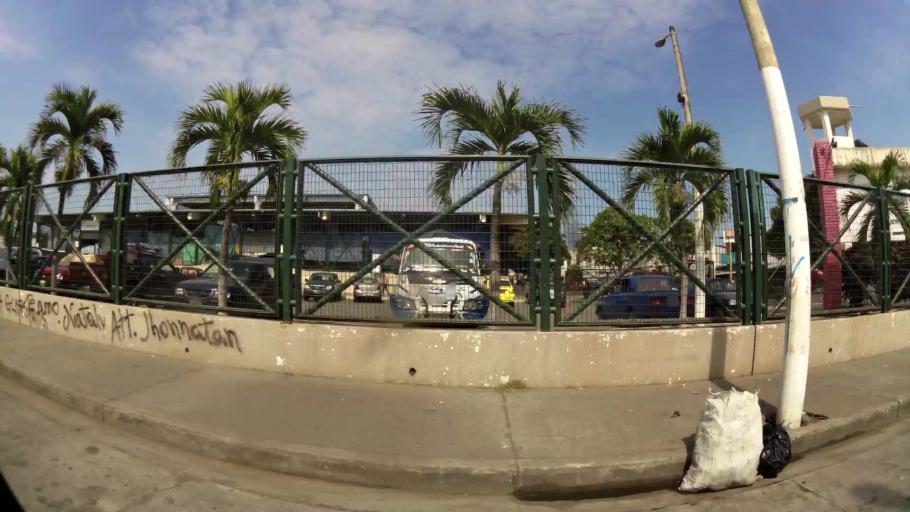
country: EC
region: Guayas
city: Guayaquil
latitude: -2.2807
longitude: -79.8803
